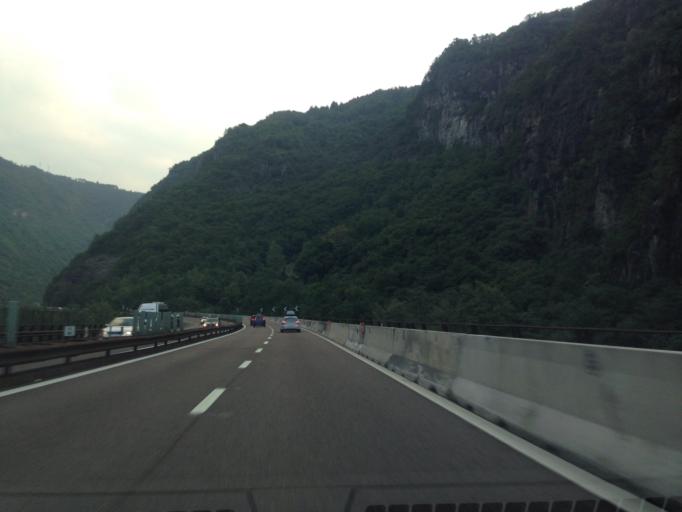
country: IT
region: Trentino-Alto Adige
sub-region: Bolzano
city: Fie Allo Sciliar
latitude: 46.5513
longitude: 11.5142
